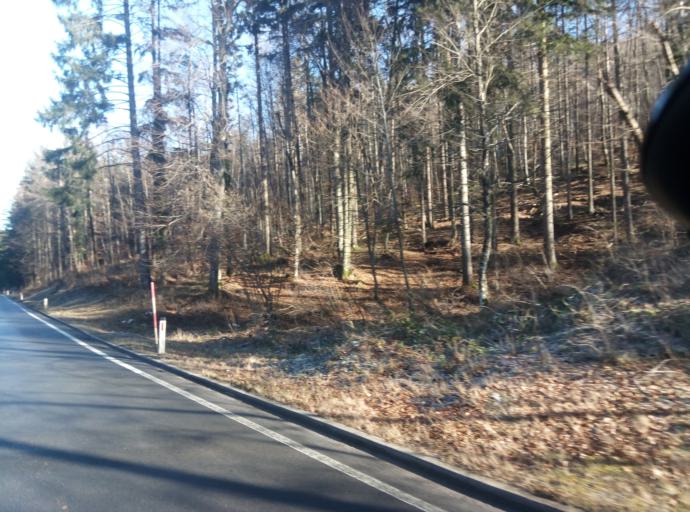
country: SI
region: Bloke
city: Nova Vas
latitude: 45.7546
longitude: 14.4665
